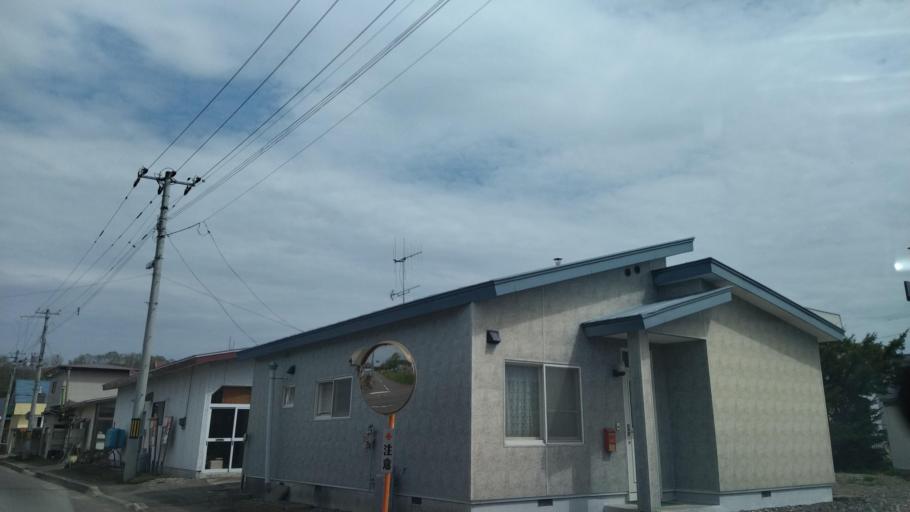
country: JP
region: Hokkaido
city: Otofuke
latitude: 43.2365
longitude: 143.5564
